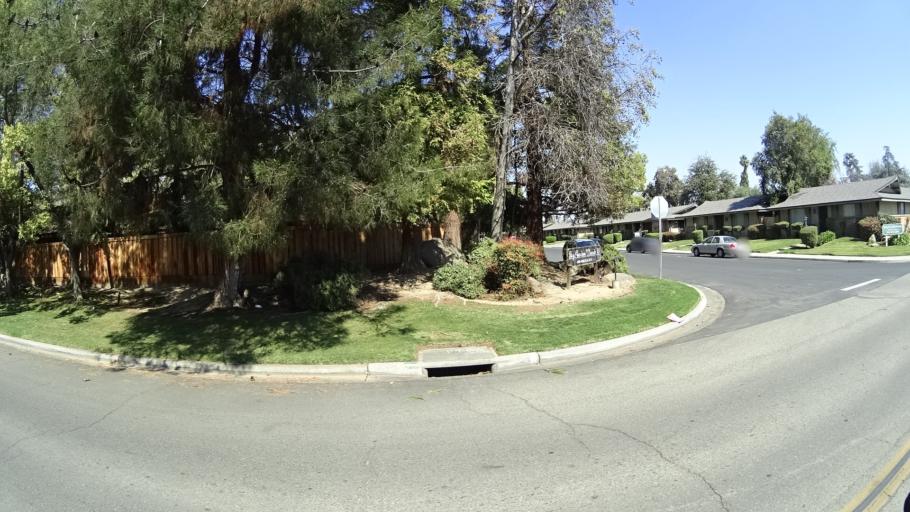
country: US
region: California
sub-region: Fresno County
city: Fresno
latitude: 36.8013
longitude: -119.7930
